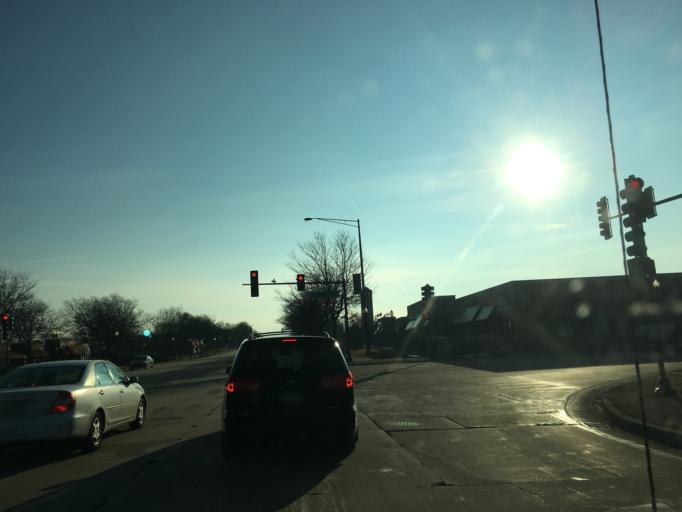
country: US
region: Illinois
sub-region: Cook County
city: Schaumburg
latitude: 42.0271
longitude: -88.0830
